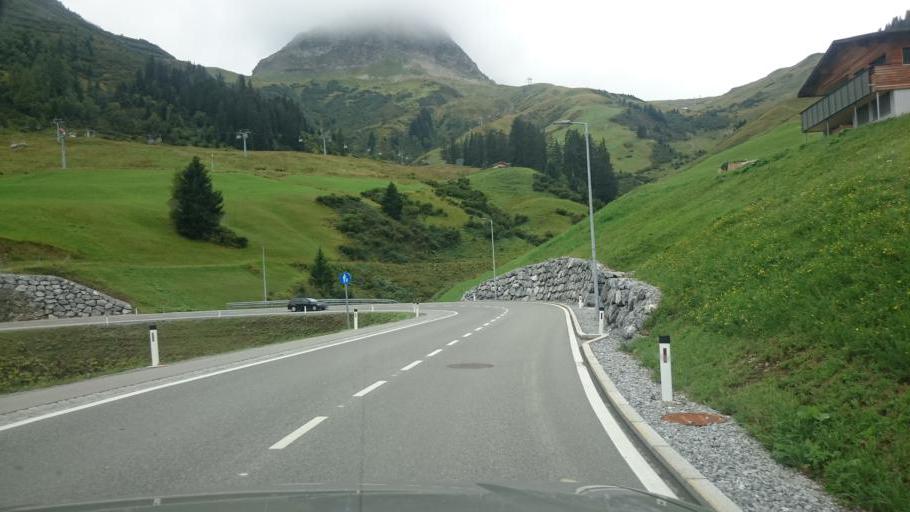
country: AT
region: Vorarlberg
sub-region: Politischer Bezirk Bregenz
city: Warth
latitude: 47.2614
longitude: 10.1744
